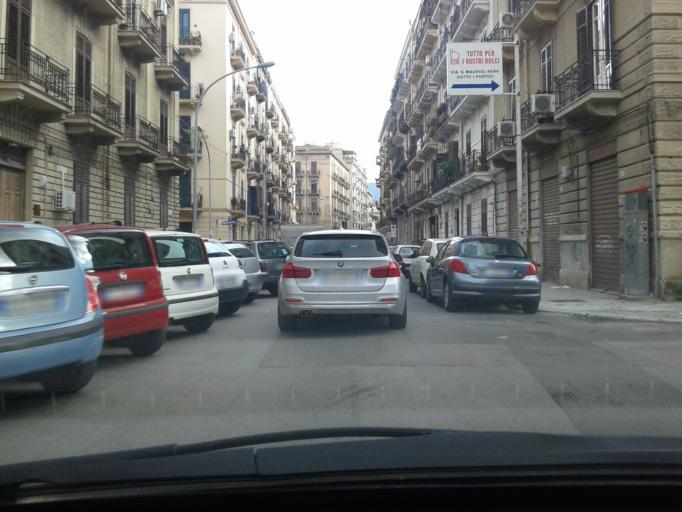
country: IT
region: Sicily
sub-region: Palermo
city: Palermo
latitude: 38.1194
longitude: 13.3450
